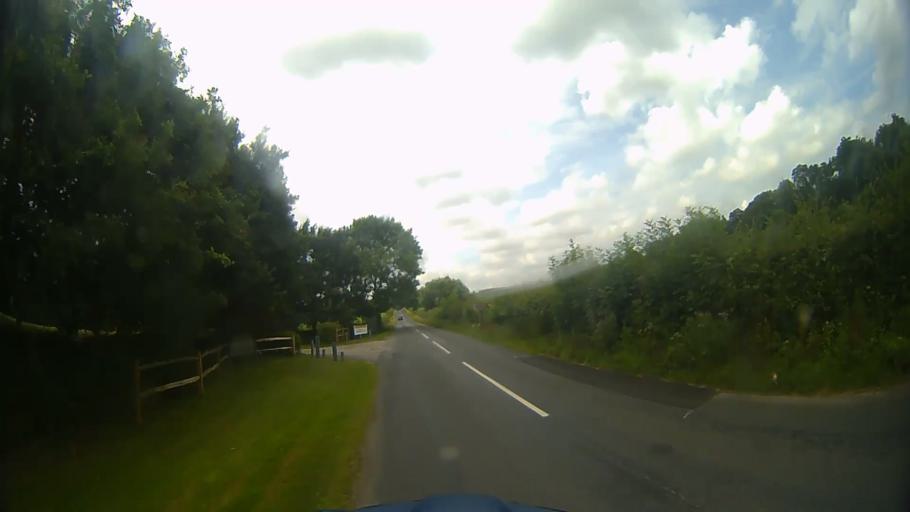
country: GB
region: England
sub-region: Hampshire
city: Kingsley
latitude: 51.1625
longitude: -0.8538
